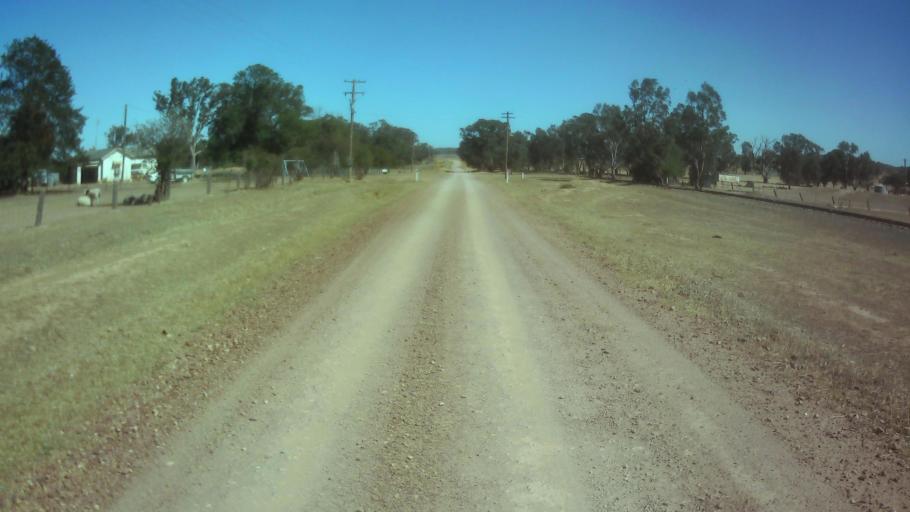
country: AU
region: New South Wales
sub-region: Weddin
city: Grenfell
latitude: -33.9448
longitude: 148.2932
